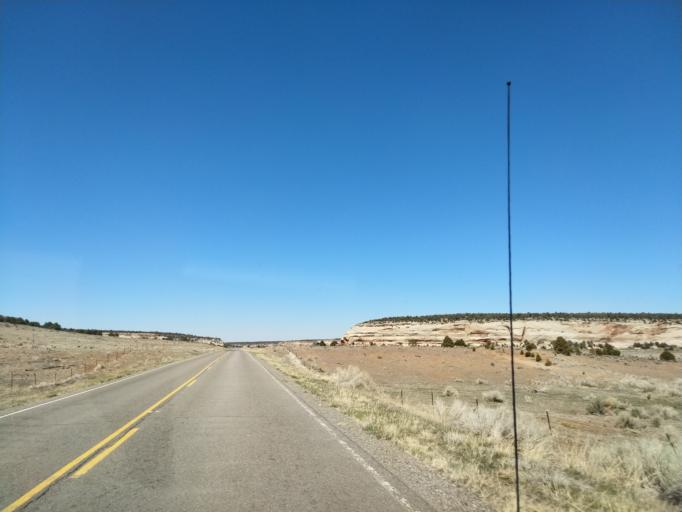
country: US
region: Colorado
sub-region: Mesa County
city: Fruita
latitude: 38.9896
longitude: -108.8161
